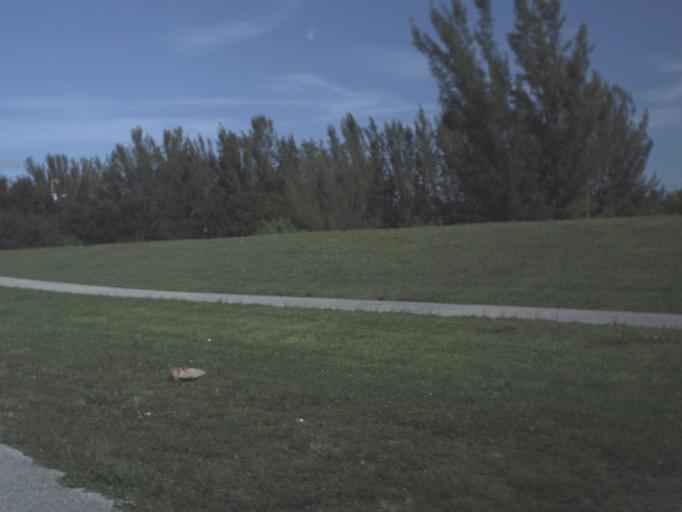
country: US
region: Florida
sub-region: Lee County
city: Cape Coral
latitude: 26.6058
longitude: -81.9833
